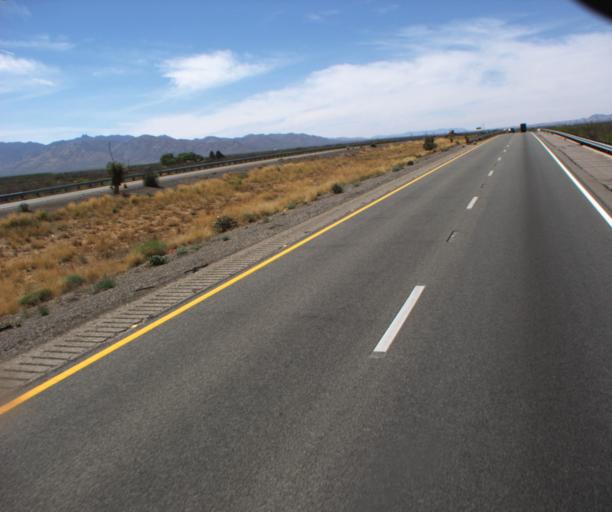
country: US
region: Arizona
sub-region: Cochise County
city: Willcox
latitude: 32.3067
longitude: -109.3942
